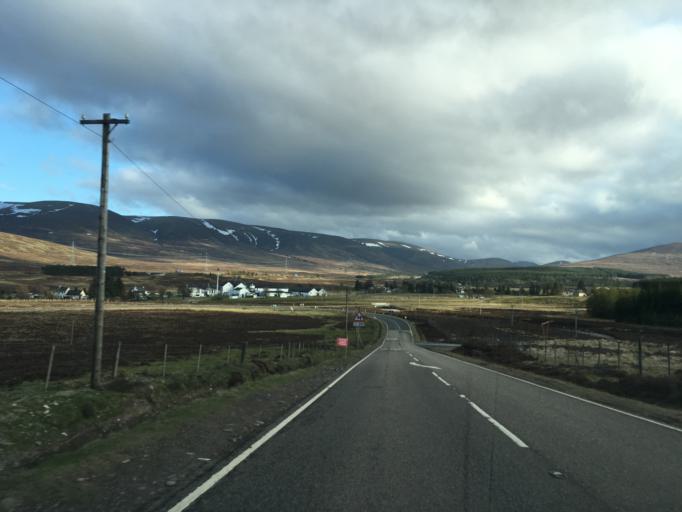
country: GB
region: Scotland
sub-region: Highland
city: Kingussie
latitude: 56.9449
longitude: -4.2430
